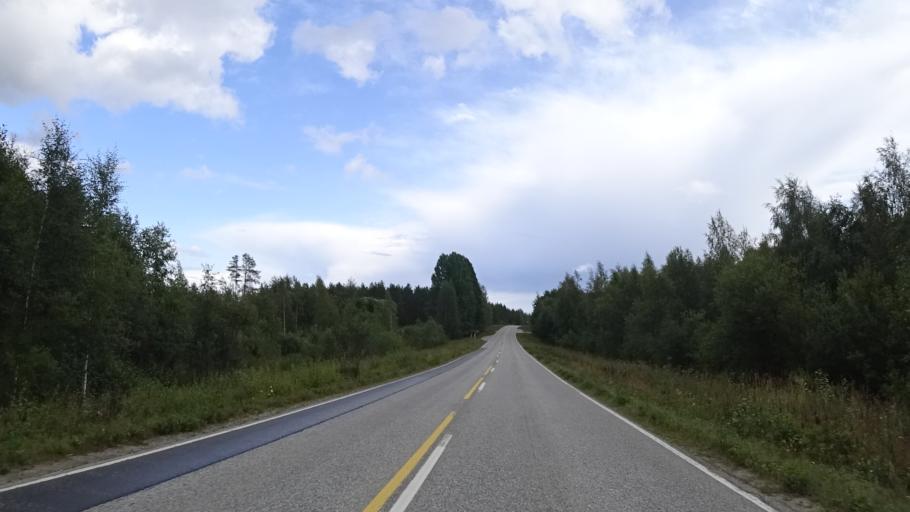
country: FI
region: North Karelia
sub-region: Joensuu
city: Ilomantsi
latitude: 62.6475
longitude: 31.0251
